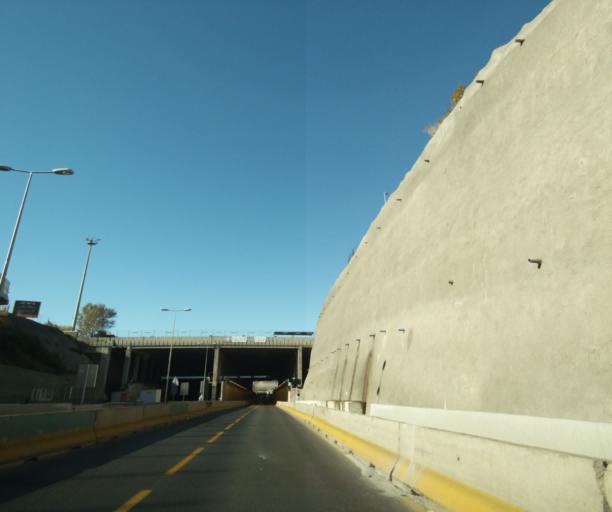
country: FR
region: Provence-Alpes-Cote d'Azur
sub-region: Departement des Bouches-du-Rhone
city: Marseille 13
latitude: 43.3300
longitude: 5.4029
